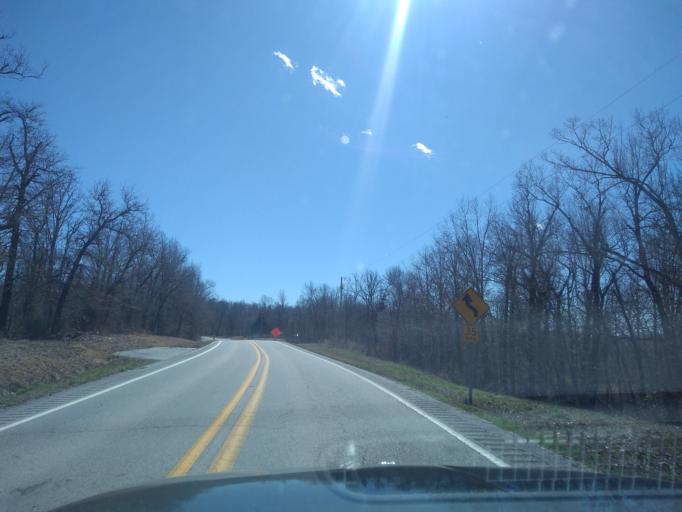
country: US
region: Arkansas
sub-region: Washington County
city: Farmington
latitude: 36.0908
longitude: -94.3313
